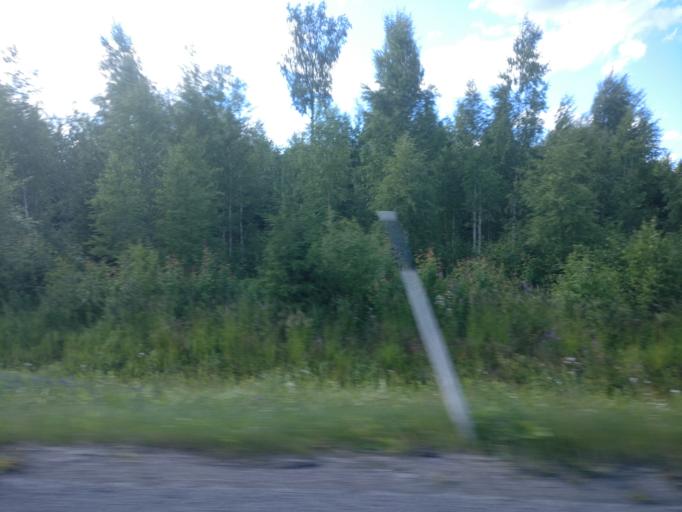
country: FI
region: Uusimaa
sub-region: Helsinki
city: Hyvinge
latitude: 60.5977
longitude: 24.8578
